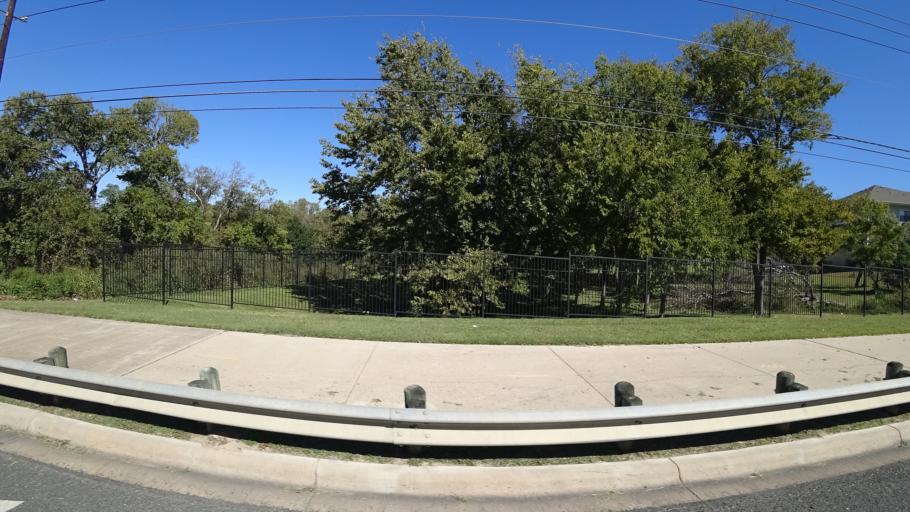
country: US
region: Texas
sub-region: Travis County
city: Hornsby Bend
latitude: 30.3020
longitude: -97.6517
